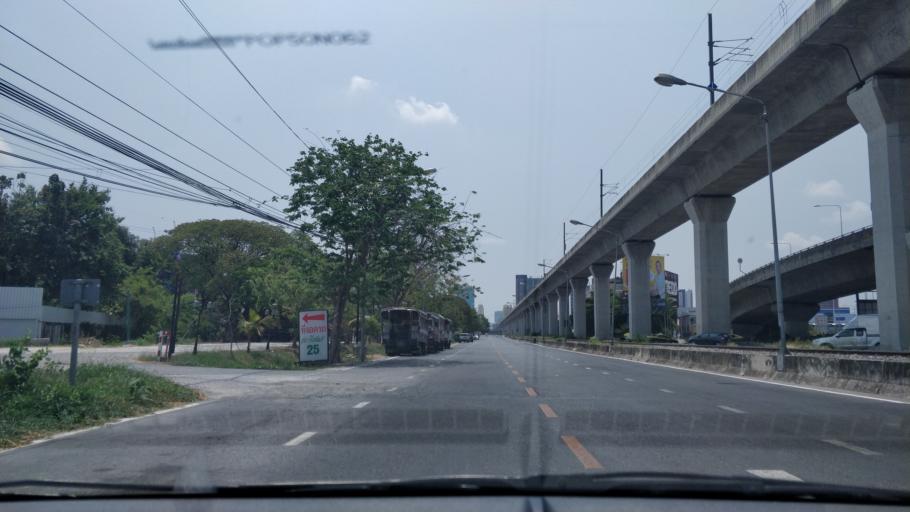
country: TH
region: Bangkok
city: Watthana
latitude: 13.7411
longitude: 100.6153
